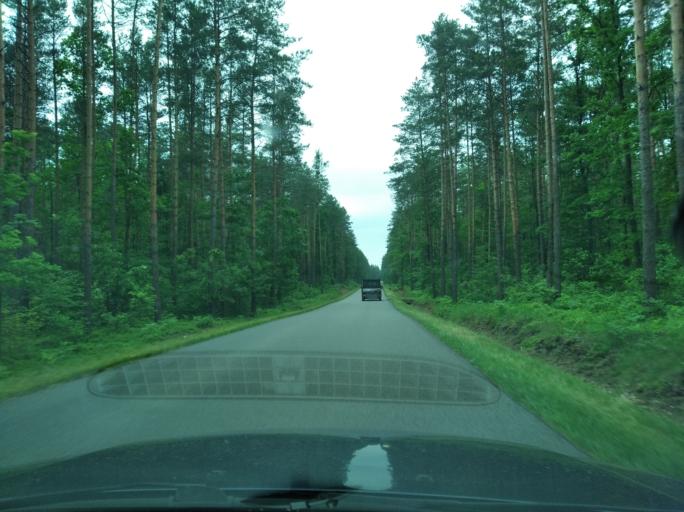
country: PL
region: Subcarpathian Voivodeship
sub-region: Powiat kolbuszowski
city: Niwiska
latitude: 50.1908
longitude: 21.6562
